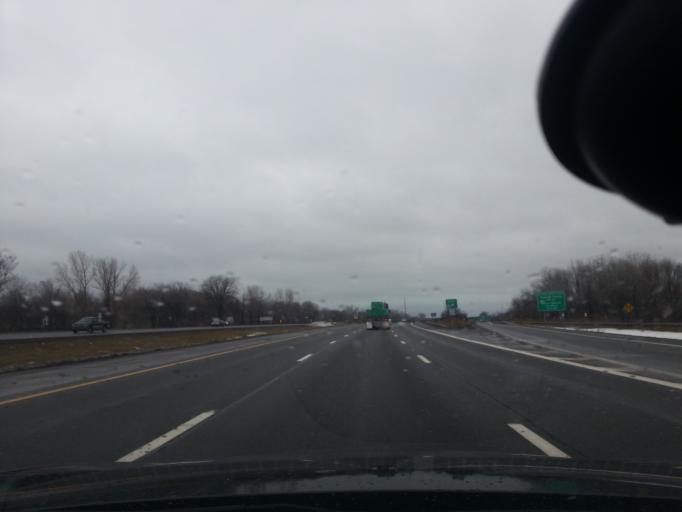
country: US
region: New York
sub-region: Onondaga County
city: North Syracuse
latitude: 43.1193
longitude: -76.1295
